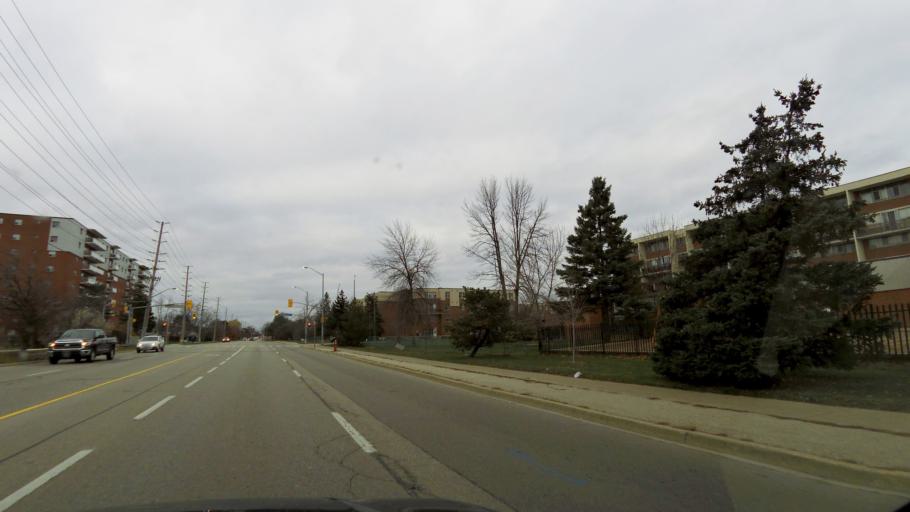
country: CA
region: Ontario
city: Mississauga
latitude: 43.5587
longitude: -79.6447
